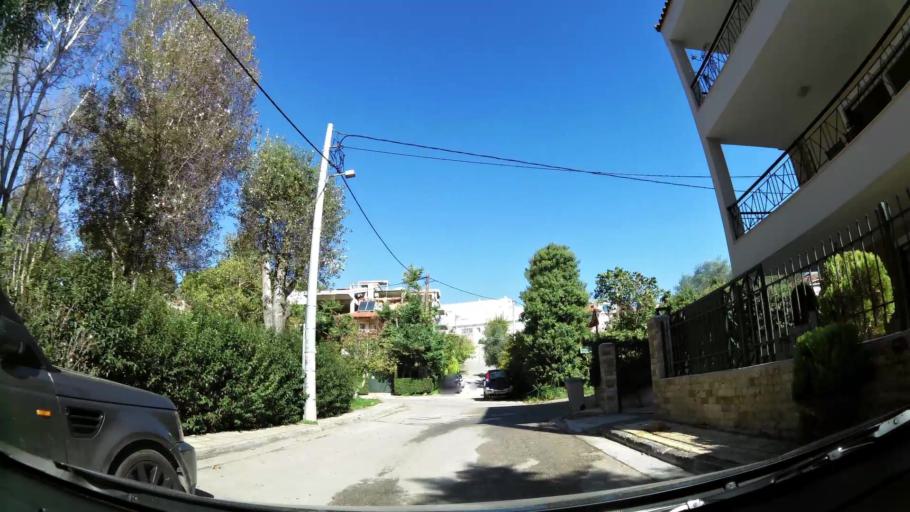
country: GR
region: Attica
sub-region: Nomarchia Anatolikis Attikis
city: Anoixi
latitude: 38.1281
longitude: 23.8596
